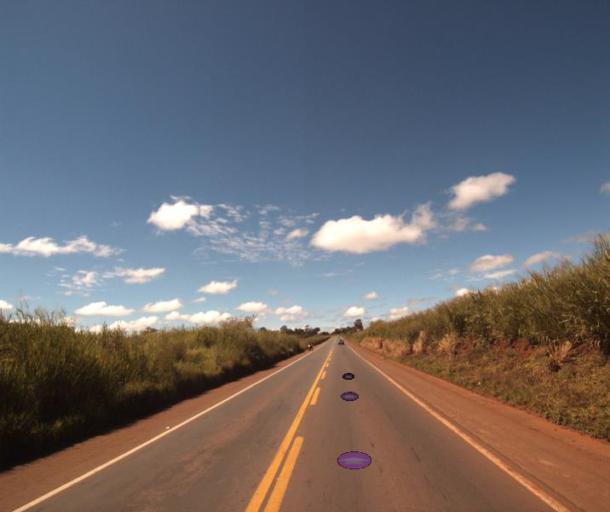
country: BR
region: Goias
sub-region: Rialma
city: Rialma
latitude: -15.3887
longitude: -49.5501
